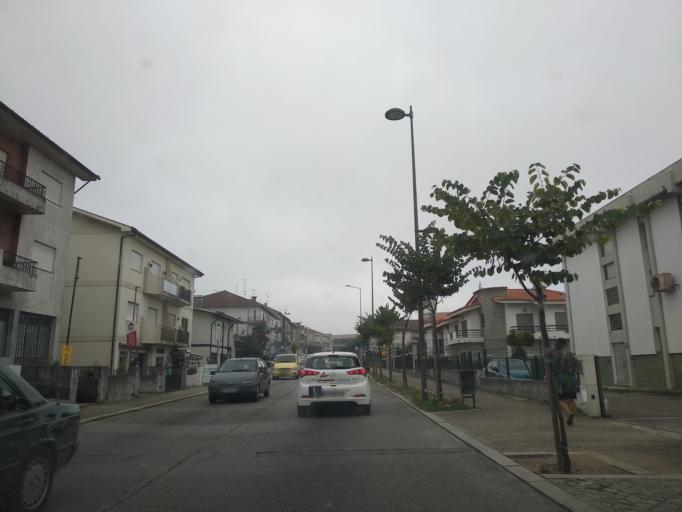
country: PT
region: Braga
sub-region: Vila Verde
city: Vila Verde
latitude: 41.6457
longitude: -8.4358
